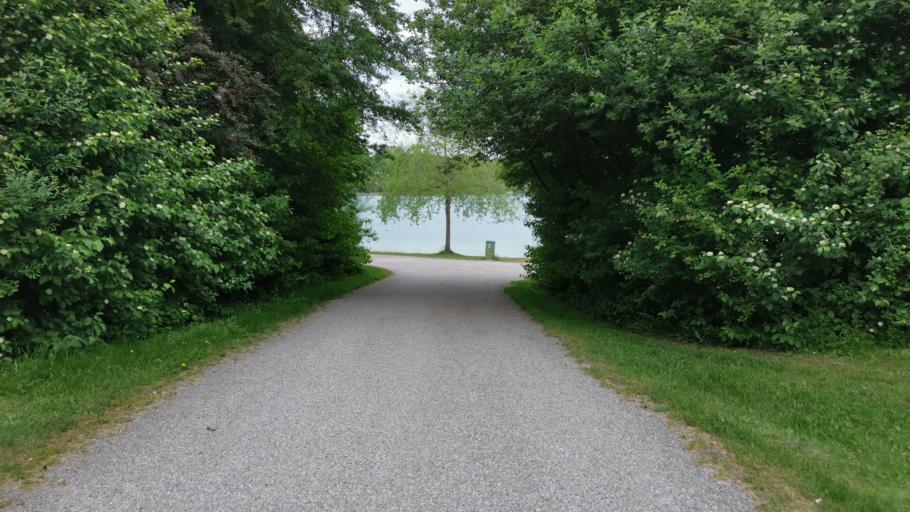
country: DE
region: Bavaria
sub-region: Upper Bavaria
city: Fuerstenfeldbruck
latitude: 48.1885
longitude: 11.2348
